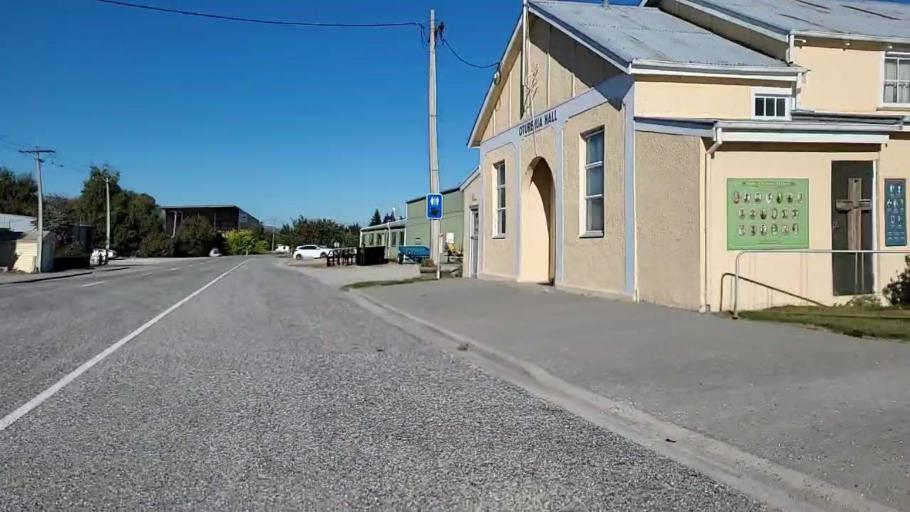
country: NZ
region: Otago
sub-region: Queenstown-Lakes District
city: Wanaka
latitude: -45.0069
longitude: 169.9129
